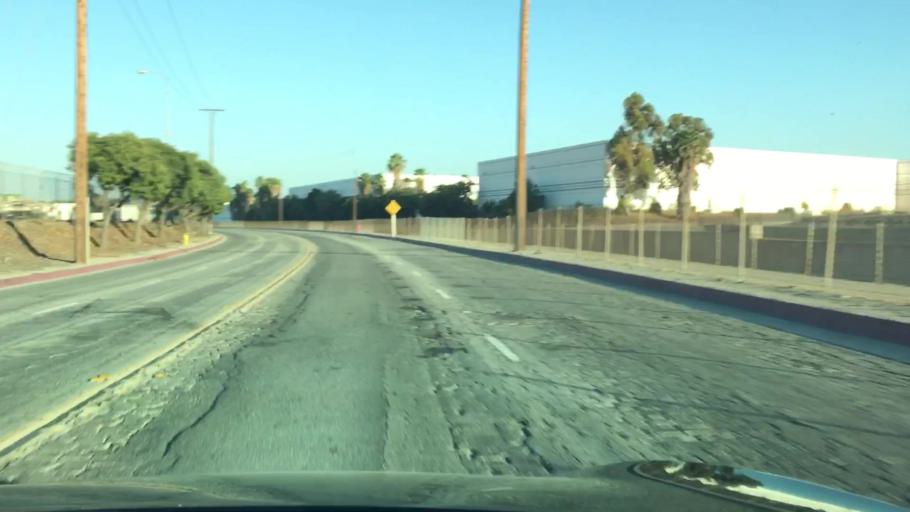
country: US
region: California
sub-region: Los Angeles County
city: South San Jose Hills
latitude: 34.0060
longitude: -117.9227
